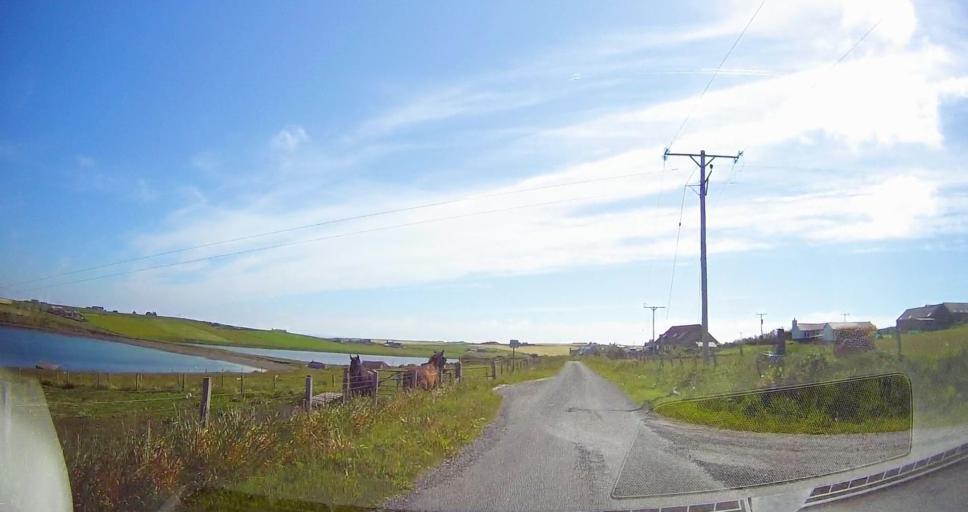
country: GB
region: Scotland
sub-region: Orkney Islands
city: Kirkwall
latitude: 58.8545
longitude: -2.9247
